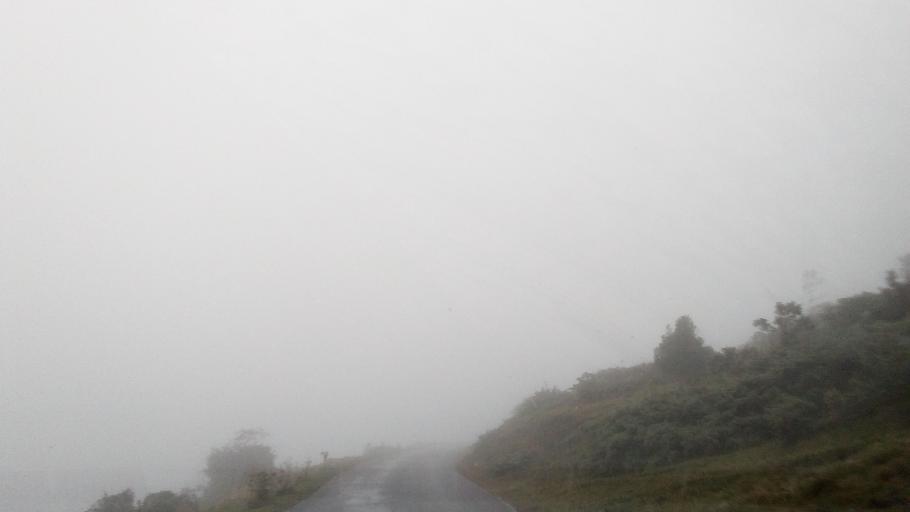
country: FR
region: Midi-Pyrenees
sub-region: Departement des Hautes-Pyrenees
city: Saint-Lary-Soulan
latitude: 42.9054
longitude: 0.3013
